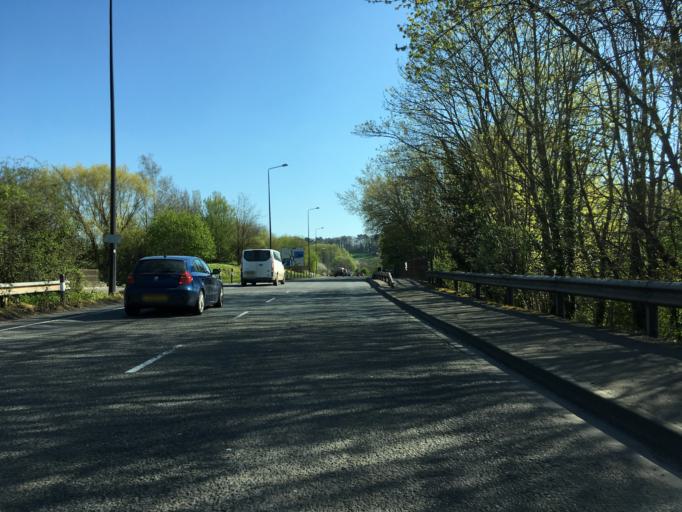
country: GB
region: England
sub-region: North Somerset
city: Easton-in-Gordano
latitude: 51.4808
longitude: -2.7121
